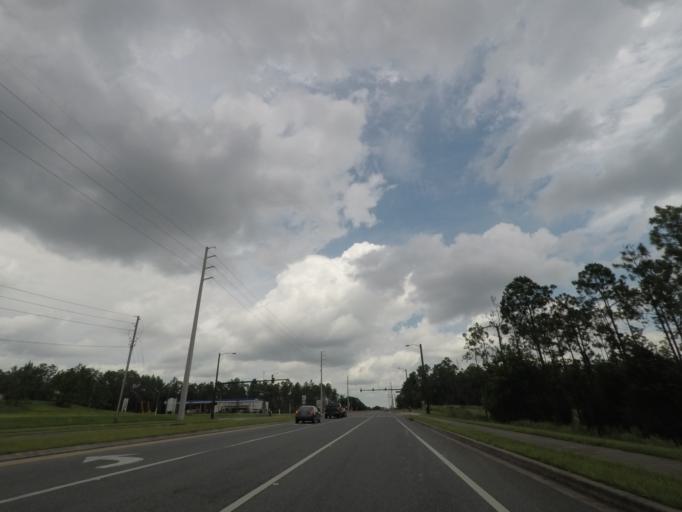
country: US
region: Florida
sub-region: Polk County
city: Loughman
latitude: 28.2952
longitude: -81.5906
